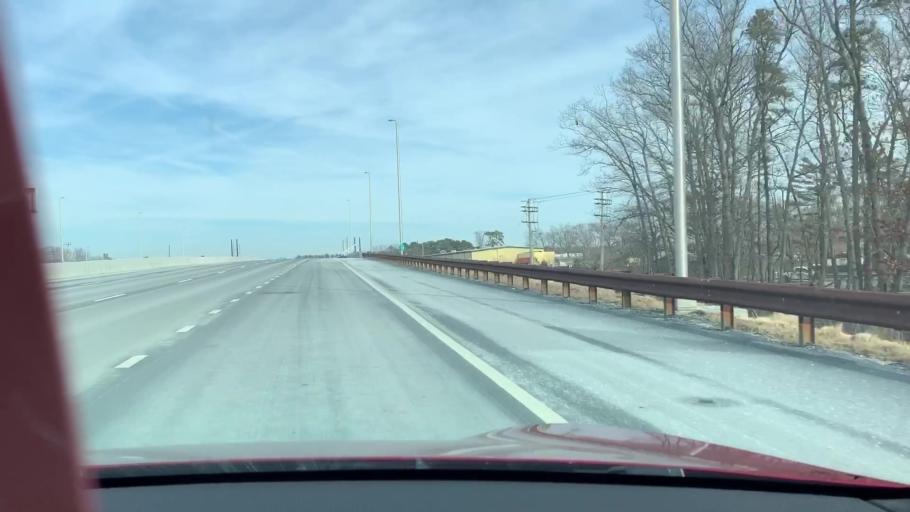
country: US
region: New Jersey
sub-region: Atlantic County
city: Northfield
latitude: 39.3971
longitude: -74.5617
